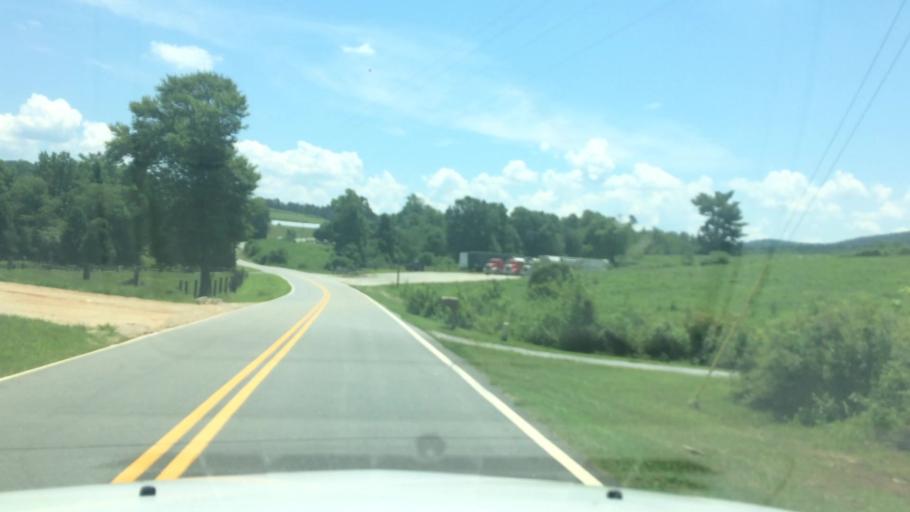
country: US
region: North Carolina
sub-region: Alexander County
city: Taylorsville
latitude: 35.9336
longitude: -81.2659
